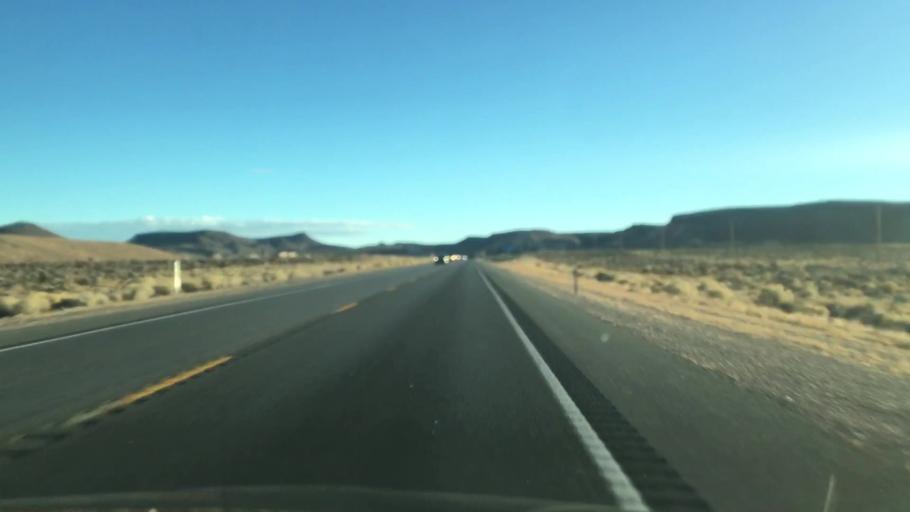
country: US
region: Nevada
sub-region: Esmeralda County
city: Goldfield
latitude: 37.7270
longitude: -117.2441
